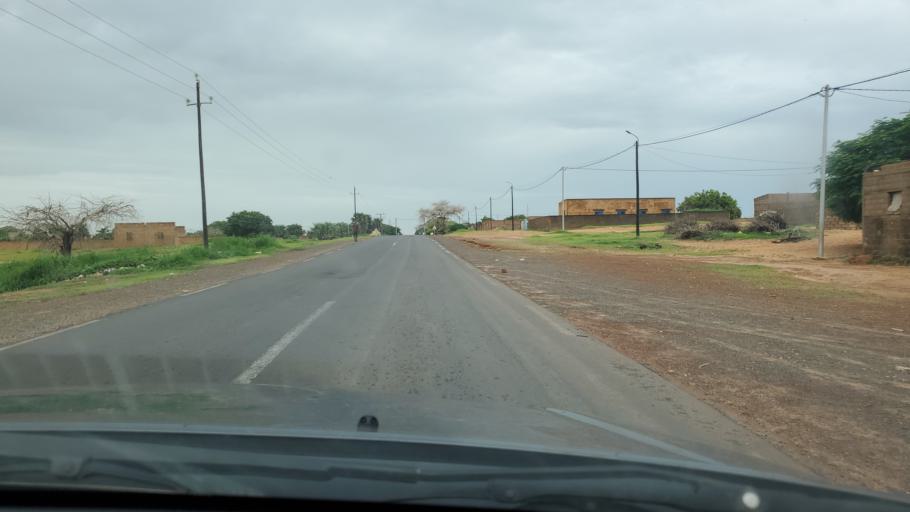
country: SN
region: Thies
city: Mekhe
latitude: 15.1362
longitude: -16.8540
